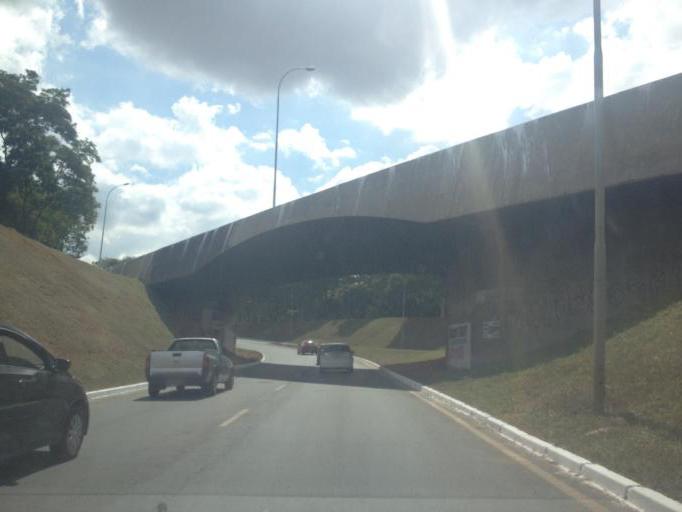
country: BR
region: Federal District
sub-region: Brasilia
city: Brasilia
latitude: -15.8331
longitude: -47.9277
